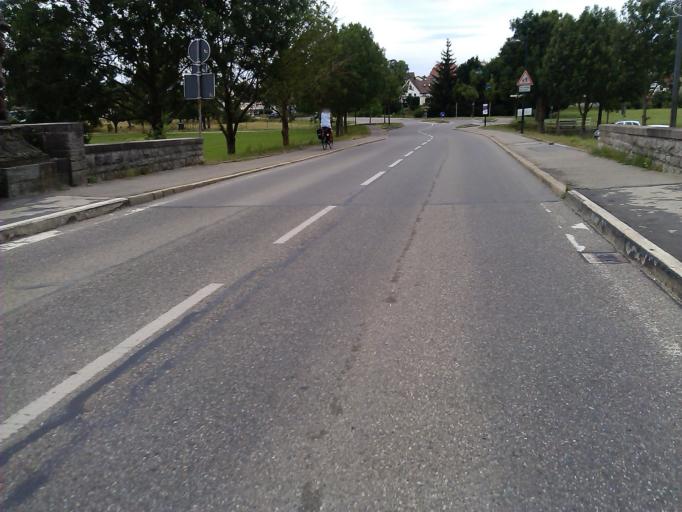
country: DE
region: Baden-Wuerttemberg
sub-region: Regierungsbezirk Stuttgart
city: Oedheim
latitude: 49.2401
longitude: 9.2511
